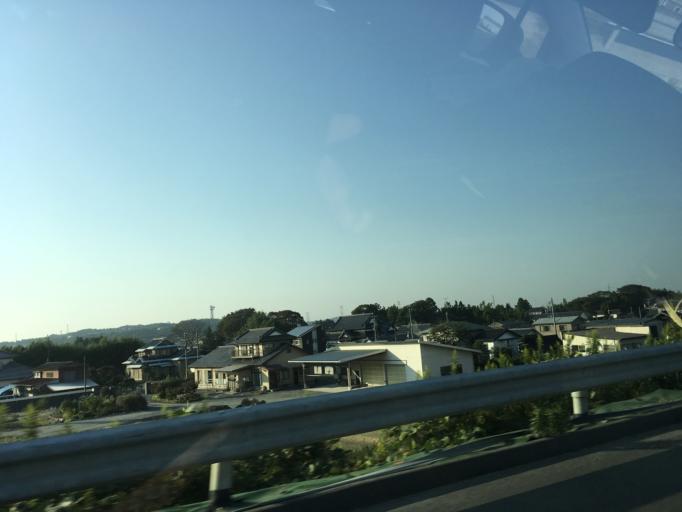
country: JP
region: Miyagi
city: Ishinomaki
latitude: 38.4515
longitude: 141.2712
